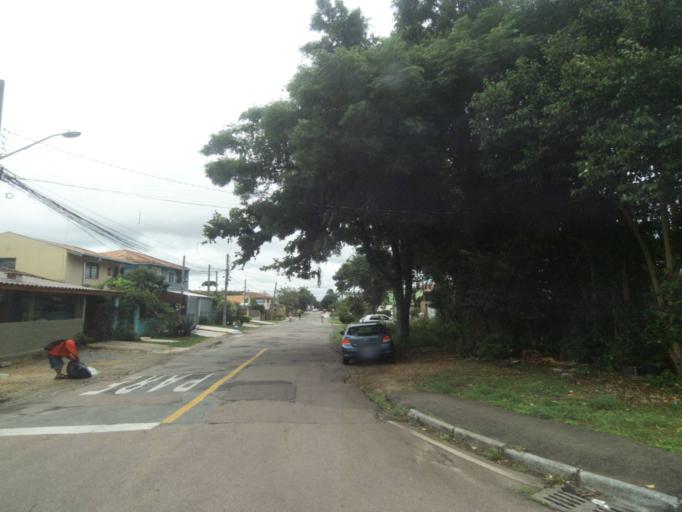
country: BR
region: Parana
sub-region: Curitiba
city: Curitiba
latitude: -25.4926
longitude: -49.3120
